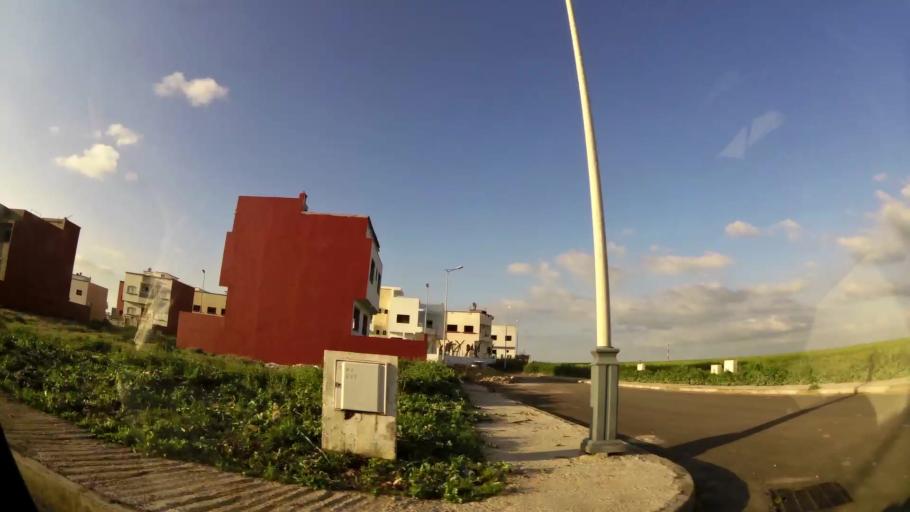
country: MA
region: Chaouia-Ouardigha
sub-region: Settat Province
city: Settat
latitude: 33.0127
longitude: -7.5988
